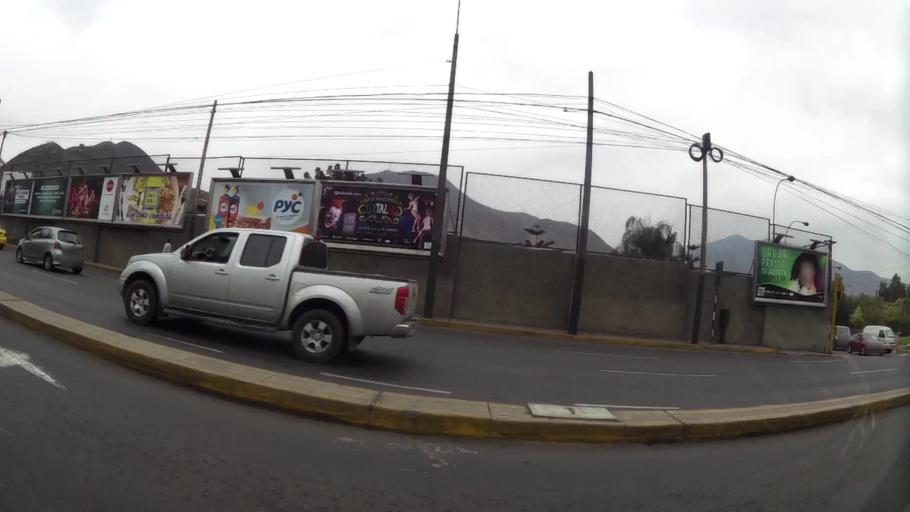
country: PE
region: Lima
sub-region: Lima
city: La Molina
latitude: -12.0947
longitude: -76.9681
